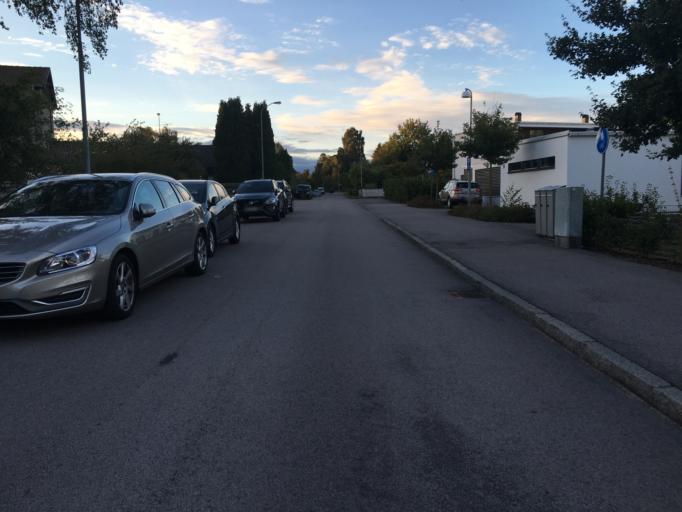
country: SE
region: Kalmar
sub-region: Kalmar Kommun
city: Kalmar
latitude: 56.6940
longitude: 16.3545
